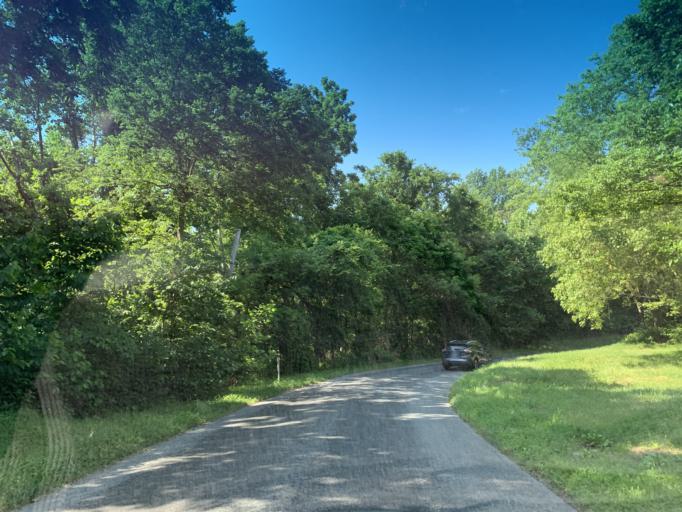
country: US
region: Maryland
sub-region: Montgomery County
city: Poolesville
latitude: 39.1300
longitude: -77.4527
